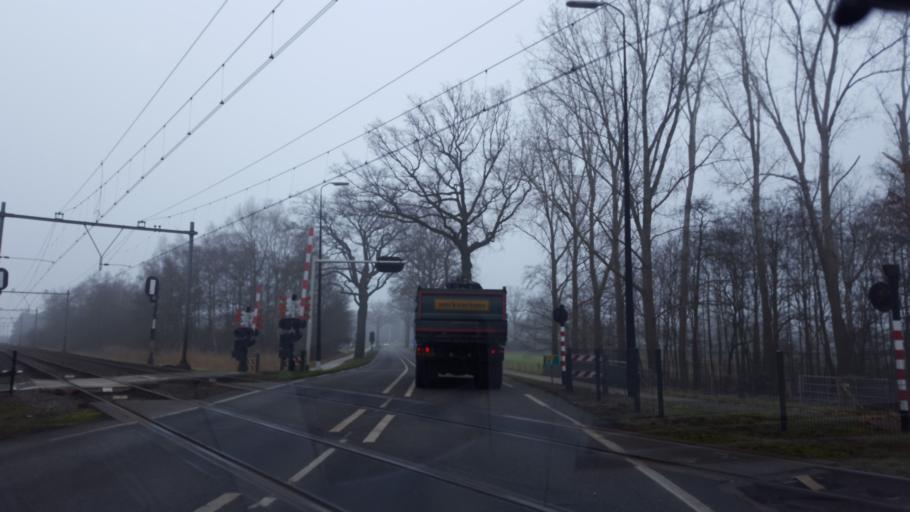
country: NL
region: Limburg
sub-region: Gemeente Nederweert
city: Nederweert
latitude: 51.2458
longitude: 5.7502
